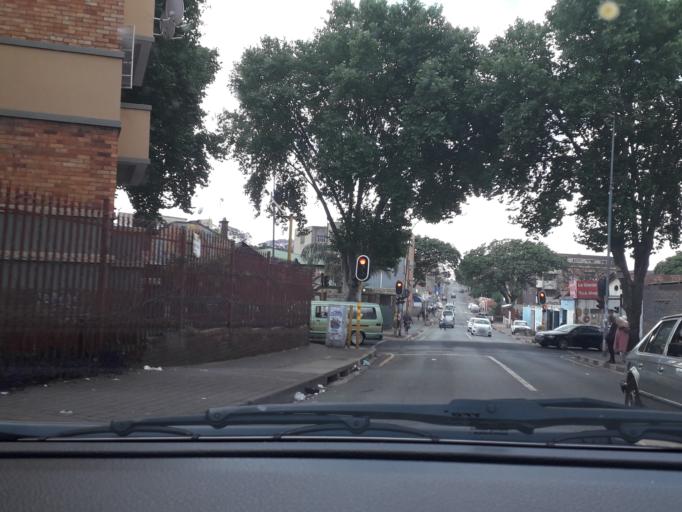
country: ZA
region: Gauteng
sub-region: City of Johannesburg Metropolitan Municipality
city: Johannesburg
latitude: -26.1809
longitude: 28.0687
